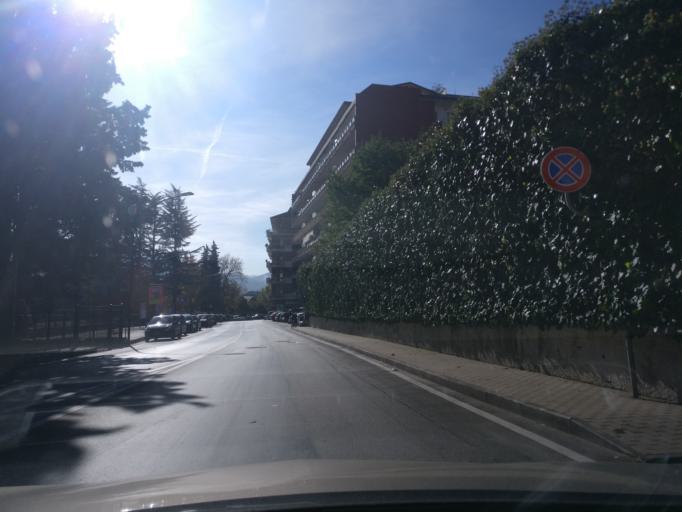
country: IT
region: Campania
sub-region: Provincia di Avellino
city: Avellino
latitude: 40.9226
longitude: 14.7817
